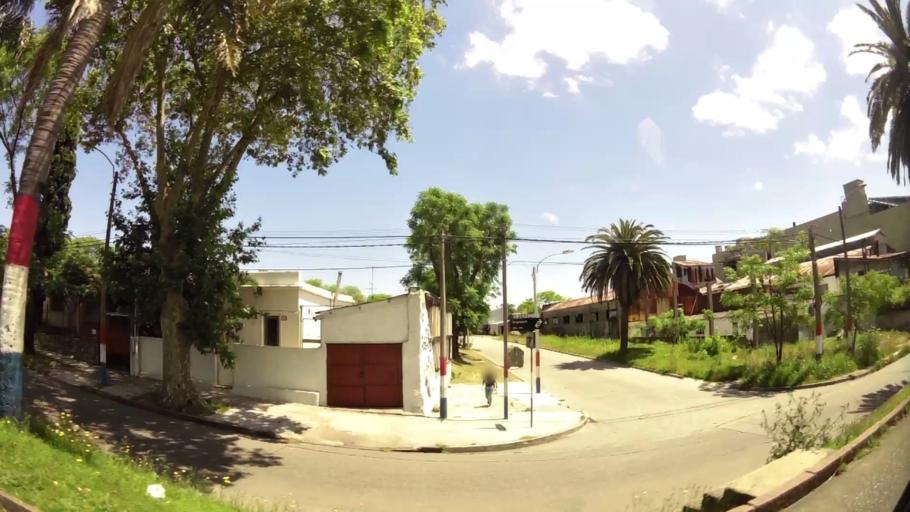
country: UY
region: Montevideo
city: Montevideo
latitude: -34.8663
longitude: -56.2125
